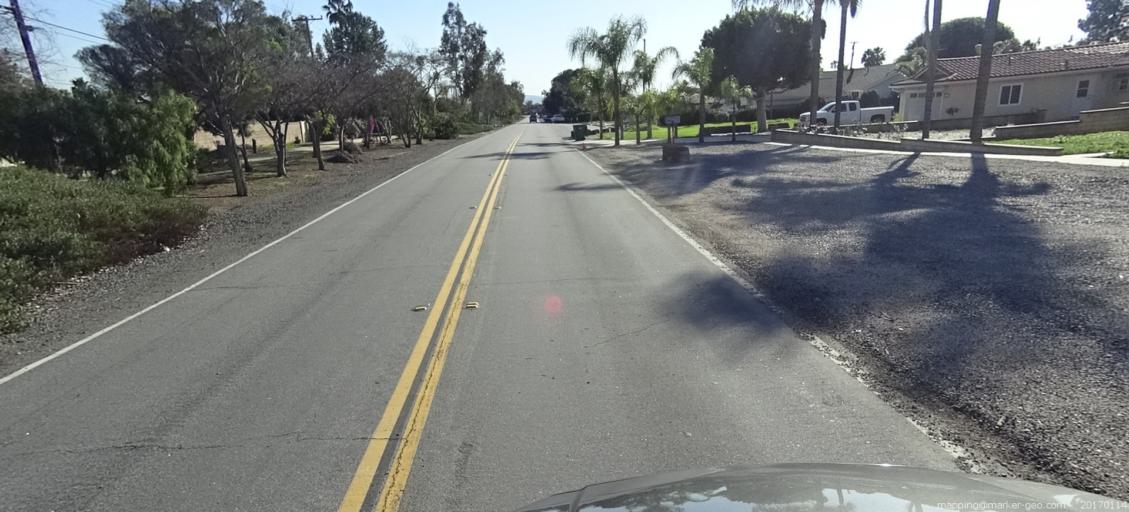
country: US
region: California
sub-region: Orange County
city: North Tustin
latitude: 33.7646
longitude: -117.8115
